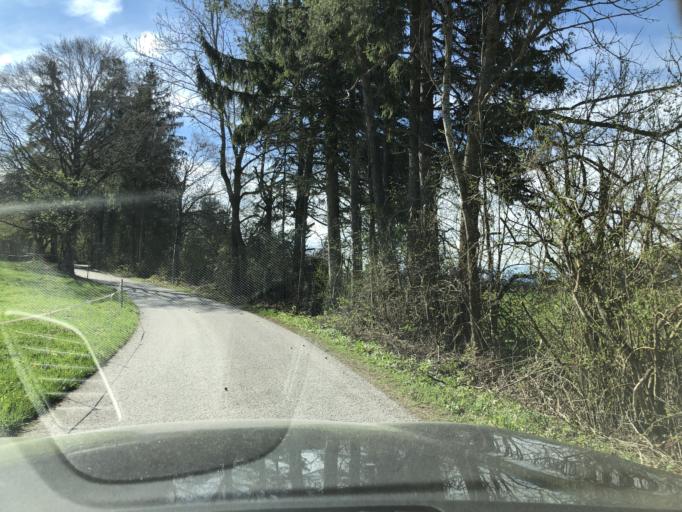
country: DE
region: Bavaria
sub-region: Swabia
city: Ruckholz
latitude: 47.6621
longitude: 10.5321
